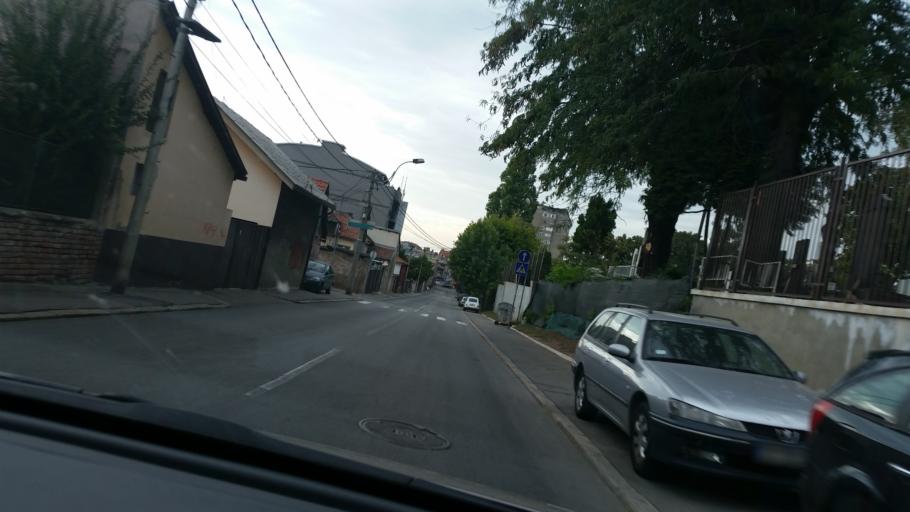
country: RS
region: Central Serbia
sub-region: Belgrade
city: Vracar
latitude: 44.8073
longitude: 20.4863
